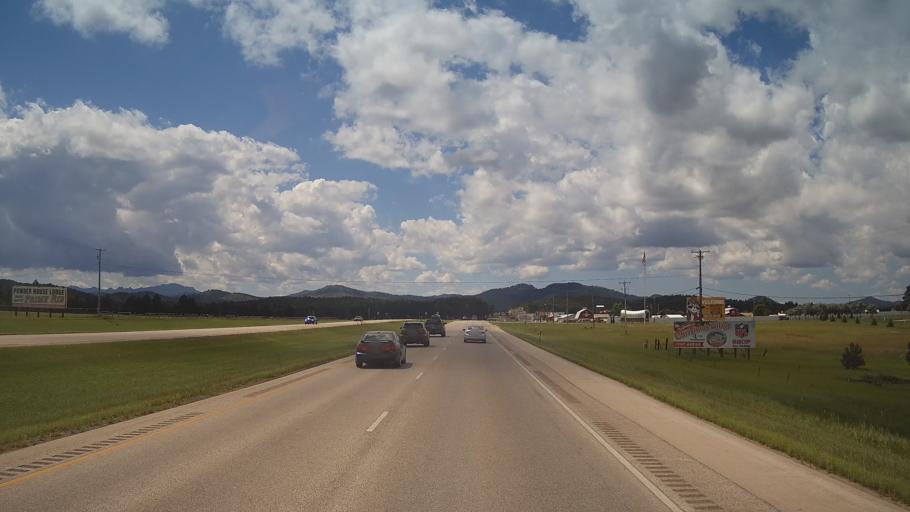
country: US
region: South Dakota
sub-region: Pennington County
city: Colonial Pine Hills
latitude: 43.9716
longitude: -103.3229
